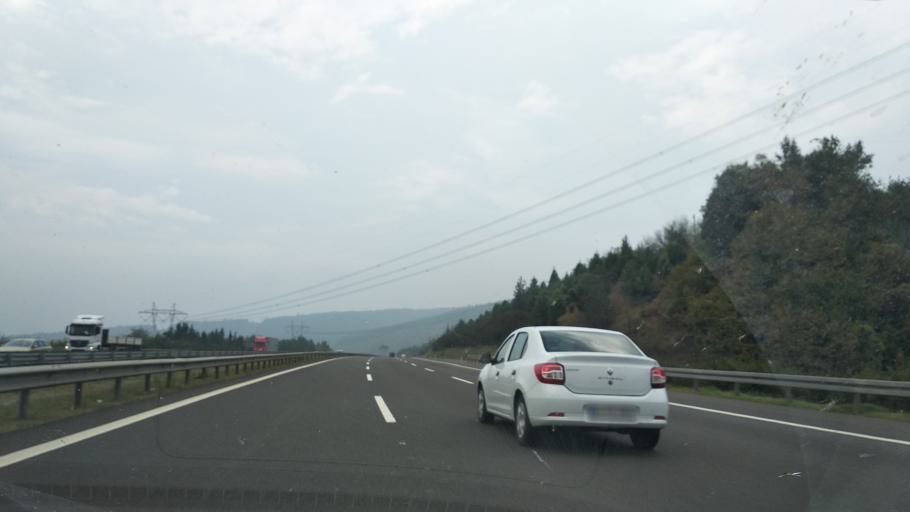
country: TR
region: Duzce
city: Kaynasli
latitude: 40.7871
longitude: 31.2953
